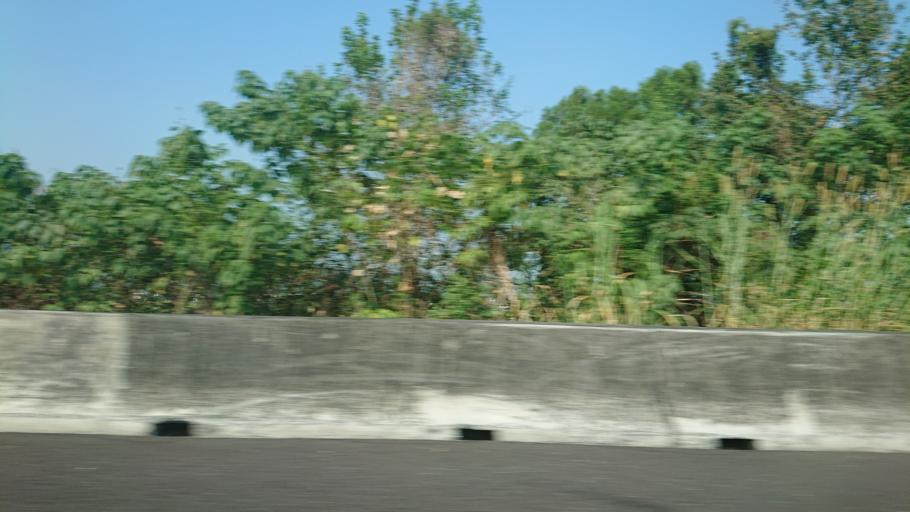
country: TW
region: Taiwan
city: Lugu
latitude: 23.8154
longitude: 120.7005
